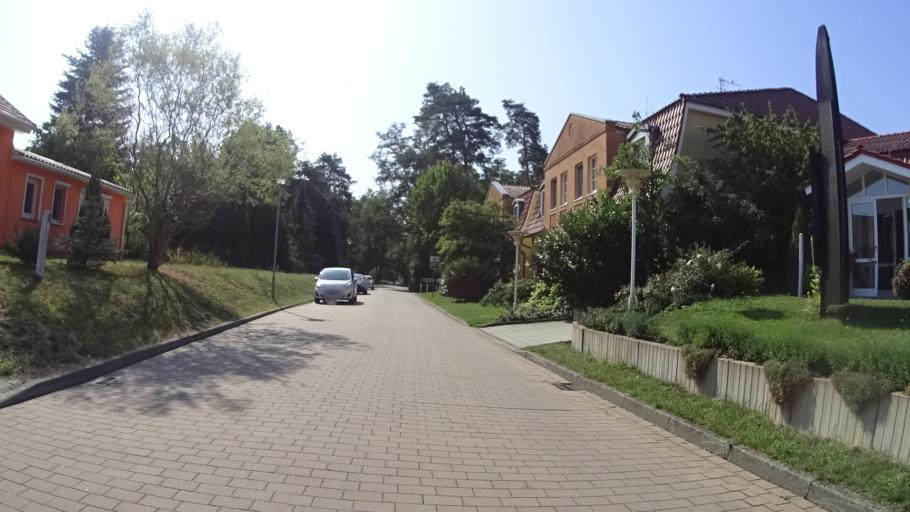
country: DE
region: Brandenburg
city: Burg
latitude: 51.8286
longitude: 14.1478
